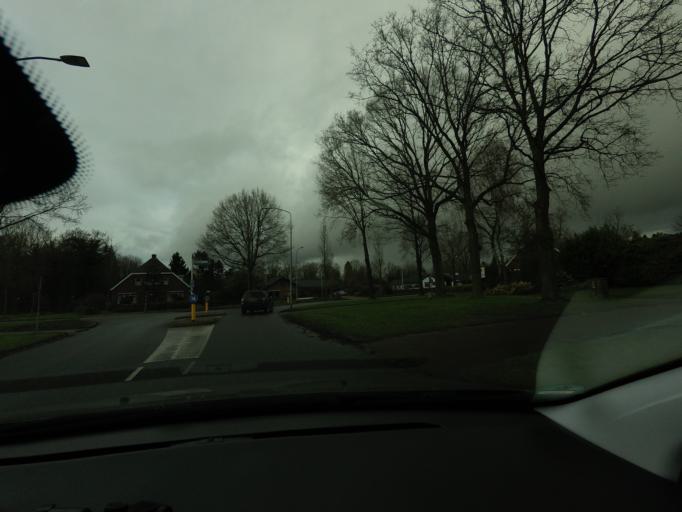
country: NL
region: Drenthe
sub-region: Gemeente Aa en Hunze
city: Anloo
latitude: 53.0025
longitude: 6.7542
